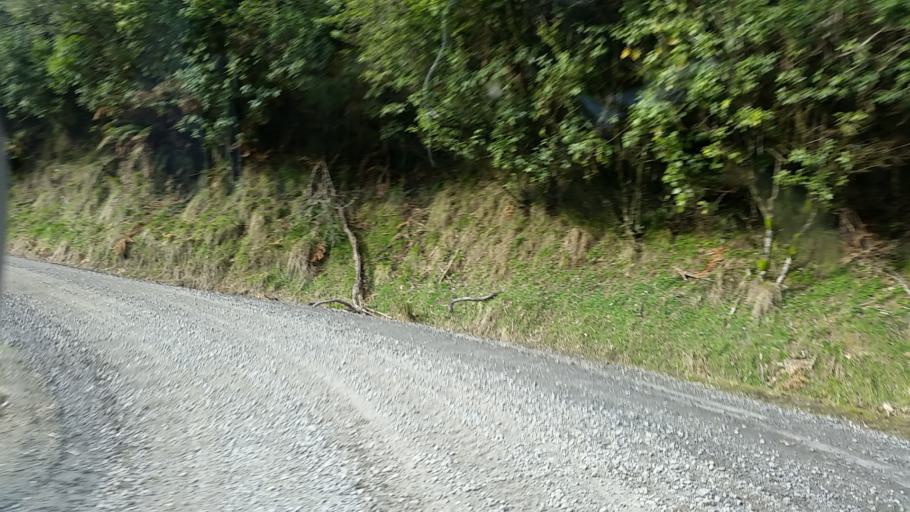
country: NZ
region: Taranaki
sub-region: South Taranaki District
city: Eltham
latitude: -39.1720
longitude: 174.6108
